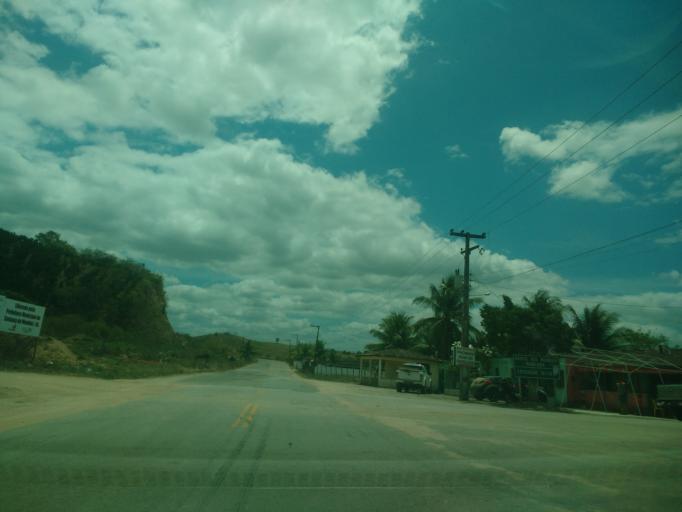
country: BR
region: Alagoas
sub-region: Santana Do Mundau
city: Santana do Mundau
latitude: -9.1406
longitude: -36.1614
